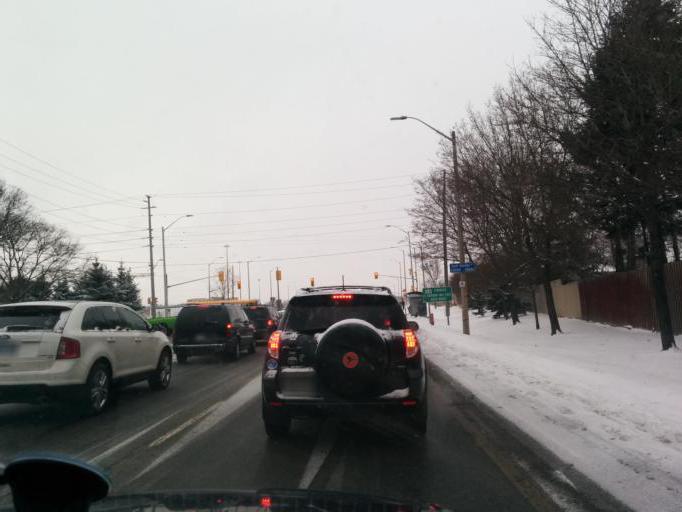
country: CA
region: Ontario
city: Mississauga
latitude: 43.5217
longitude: -79.6442
